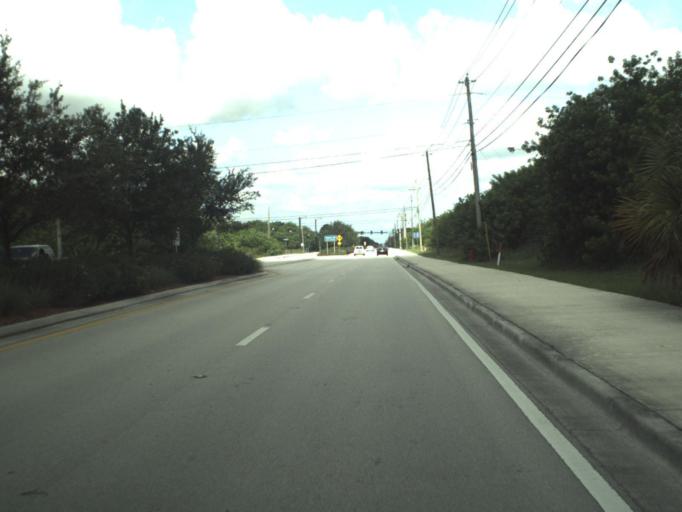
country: US
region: Florida
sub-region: Martin County
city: North River Shores
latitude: 27.2095
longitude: -80.3377
